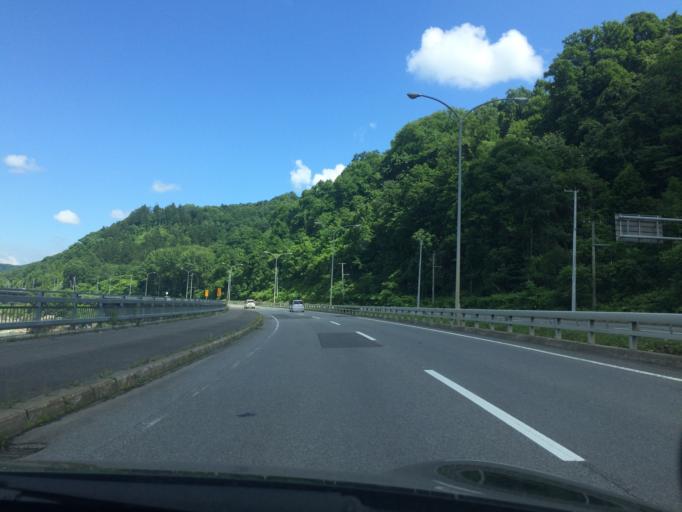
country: JP
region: Hokkaido
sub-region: Asahikawa-shi
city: Asahikawa
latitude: 43.7262
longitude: 142.2157
